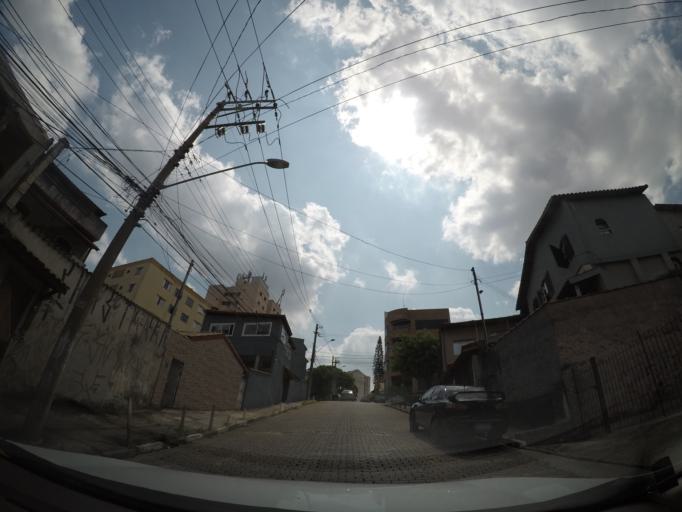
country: BR
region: Sao Paulo
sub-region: Guarulhos
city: Guarulhos
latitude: -23.4684
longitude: -46.5361
